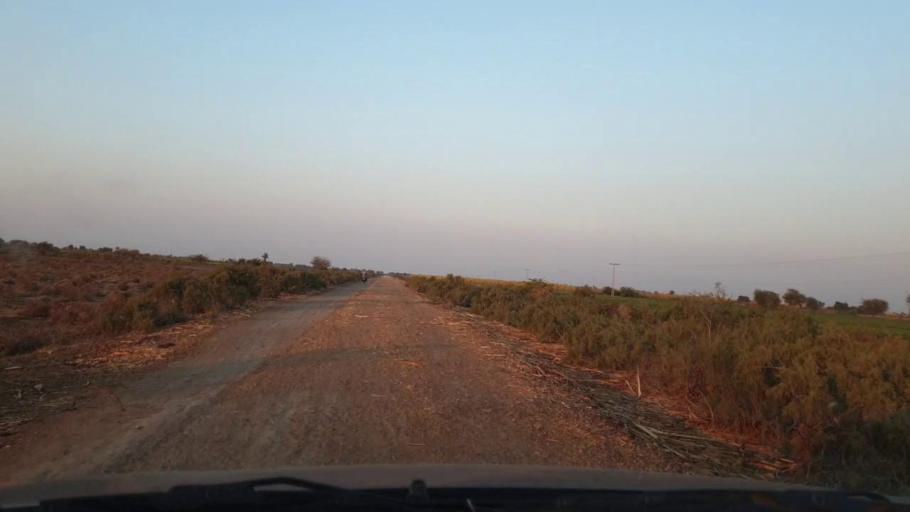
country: PK
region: Sindh
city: Jhol
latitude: 25.9236
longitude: 68.9644
